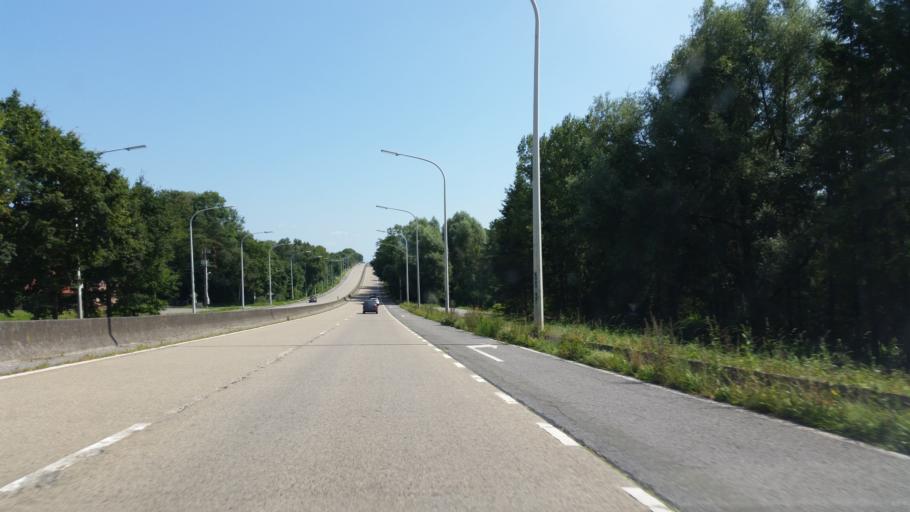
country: BE
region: Wallonia
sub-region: Province de Namur
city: Hamois
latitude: 50.2803
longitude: 5.2025
